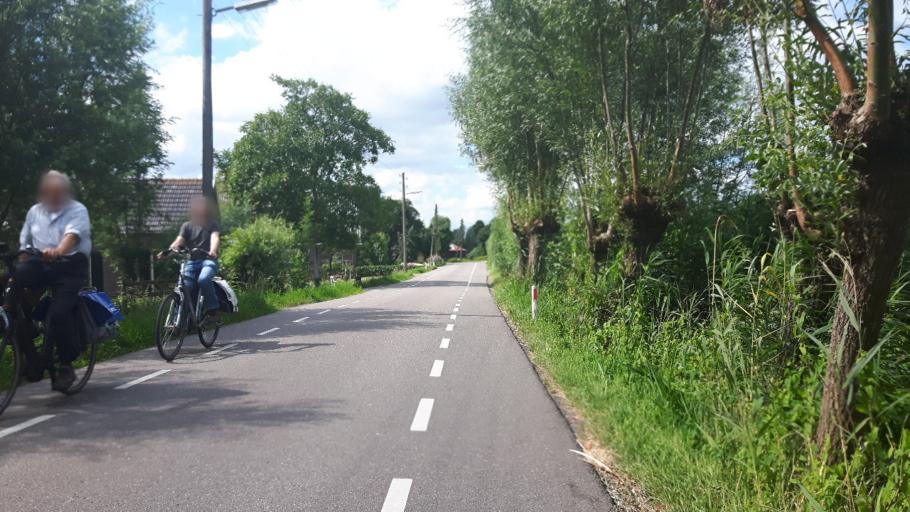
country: NL
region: South Holland
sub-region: Gemeente Vlist
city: Vlist
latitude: 51.9833
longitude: 4.8141
